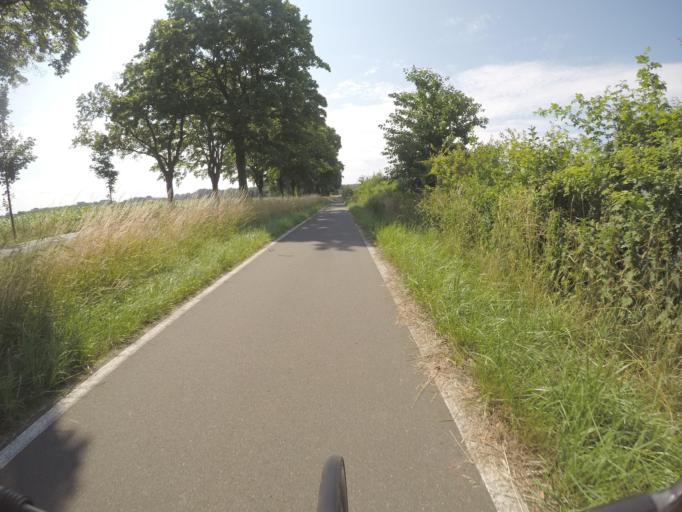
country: DE
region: Mecklenburg-Vorpommern
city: Gingst
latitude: 54.4420
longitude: 13.2225
